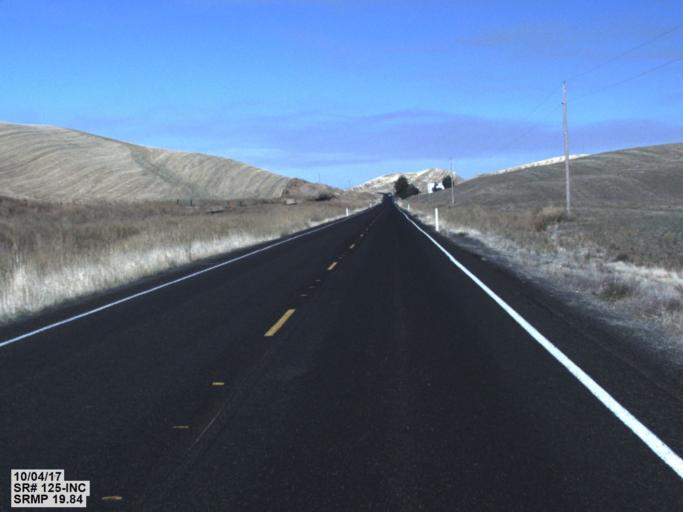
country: US
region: Washington
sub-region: Walla Walla County
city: Walla Walla
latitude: 46.2468
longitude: -118.3634
